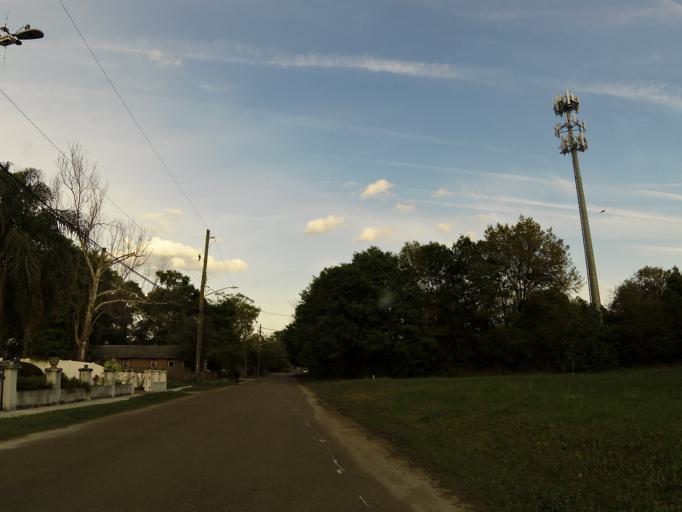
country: US
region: Florida
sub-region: Duval County
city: Jacksonville
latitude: 30.3546
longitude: -81.6775
